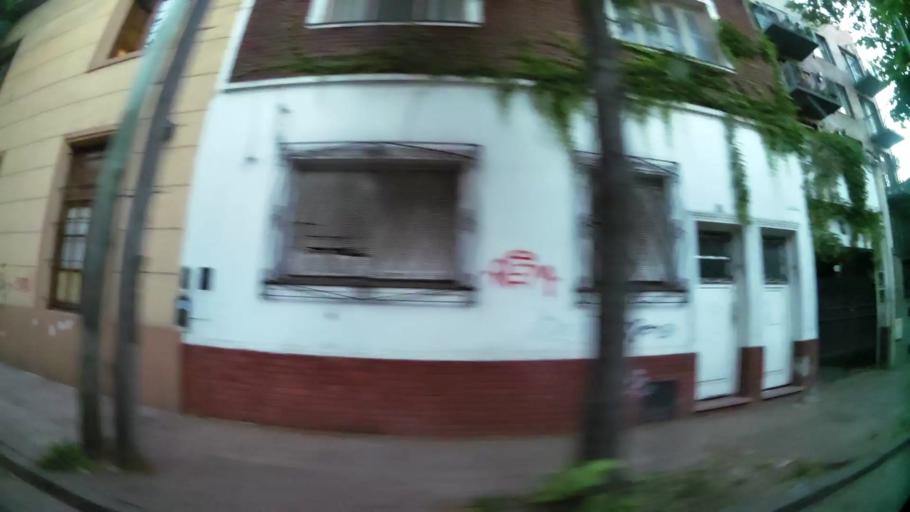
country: AR
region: Buenos Aires
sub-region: Partido de Tigre
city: Tigre
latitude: -34.4393
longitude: -58.5622
